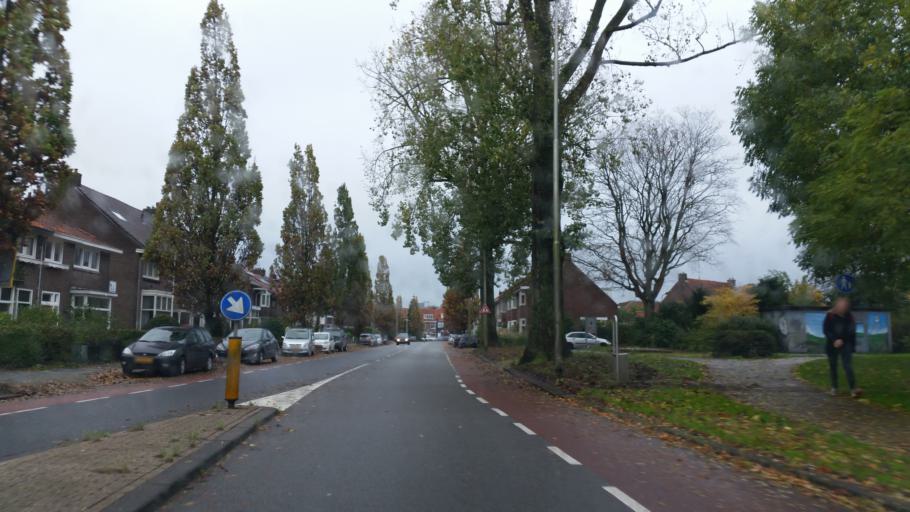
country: NL
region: Friesland
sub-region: Gemeente Leeuwarden
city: Leeuwarden
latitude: 53.2052
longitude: 5.8068
